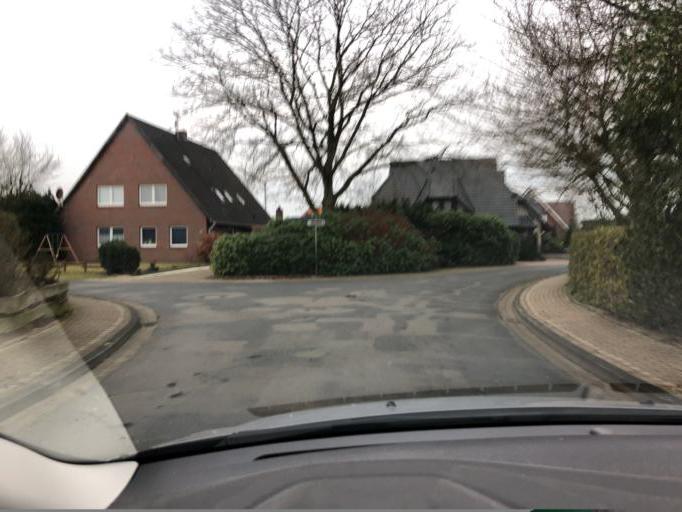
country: DE
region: Lower Saxony
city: Bad Zwischenahn
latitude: 53.1787
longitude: 8.0248
